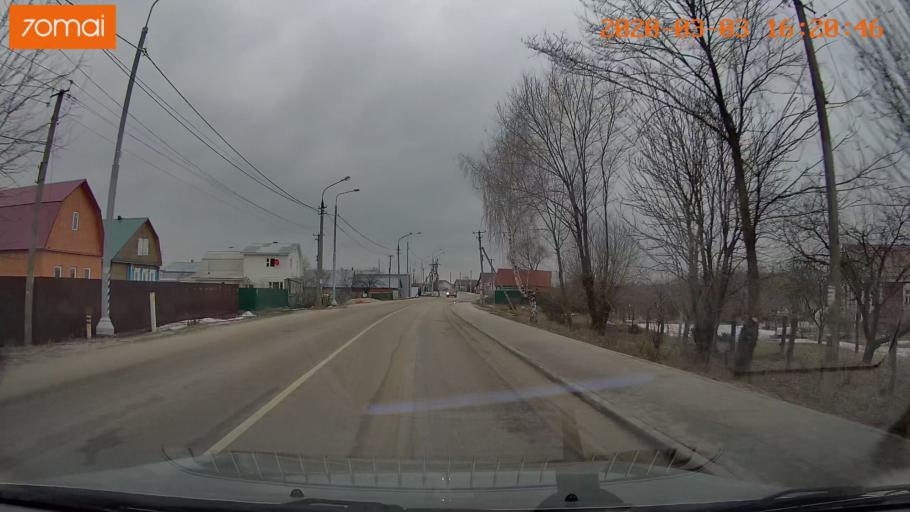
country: RU
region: Moskovskaya
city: Imeni Tsyurupy
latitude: 55.4966
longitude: 38.6543
